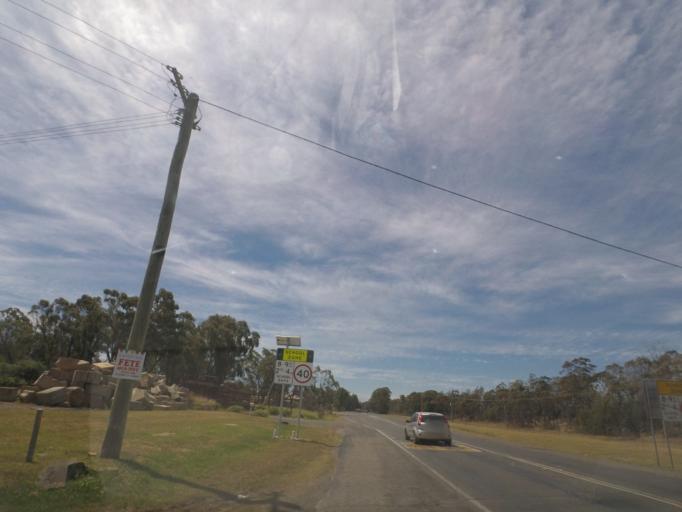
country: AU
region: New South Wales
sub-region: Wollondilly
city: Buxton
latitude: -34.2547
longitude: 150.5743
